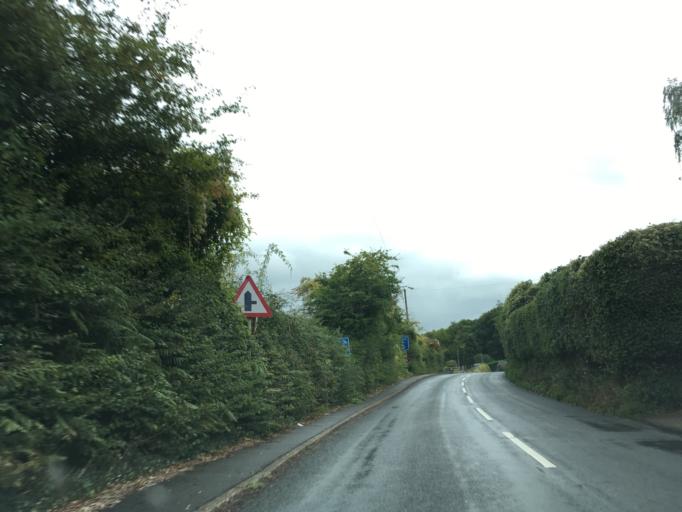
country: GB
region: Wales
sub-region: Monmouthshire
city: Abergavenny
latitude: 51.8196
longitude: -3.0526
